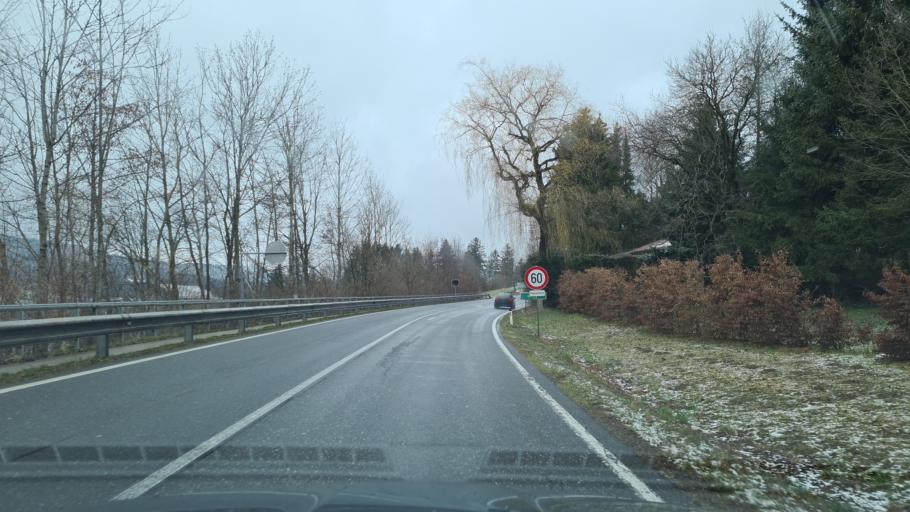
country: AT
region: Upper Austria
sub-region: Politischer Bezirk Vocklabruck
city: Zell am Moos
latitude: 47.8957
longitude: 13.3144
